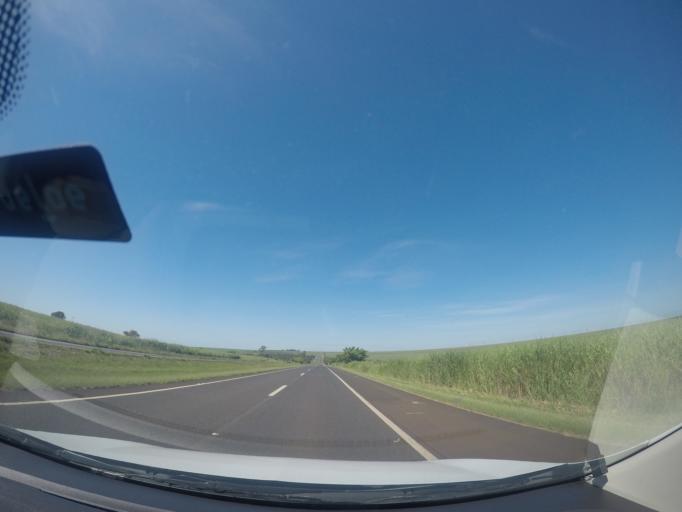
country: BR
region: Goias
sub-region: Morrinhos
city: Morrinhos
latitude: -17.8694
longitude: -49.2260
